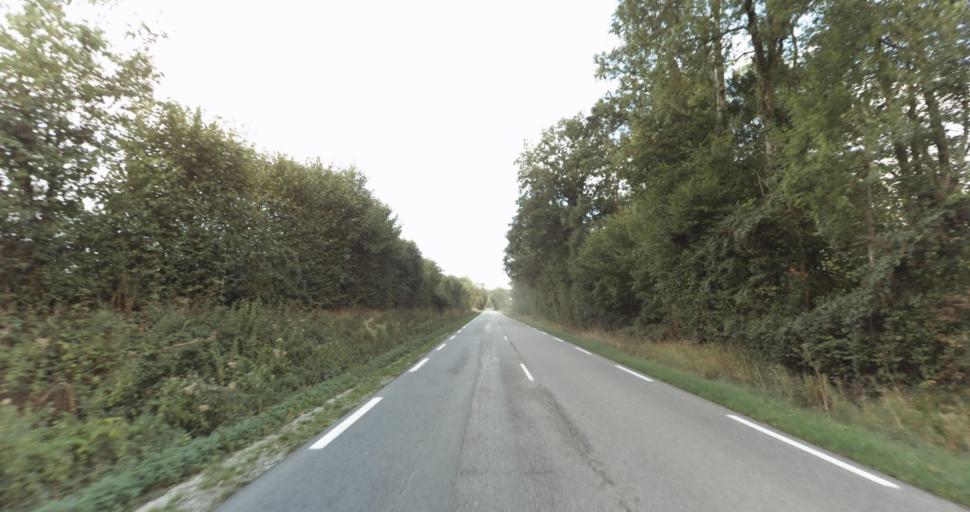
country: FR
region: Lower Normandy
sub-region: Departement de l'Orne
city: Sainte-Gauburge-Sainte-Colombe
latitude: 48.7252
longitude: 0.4159
